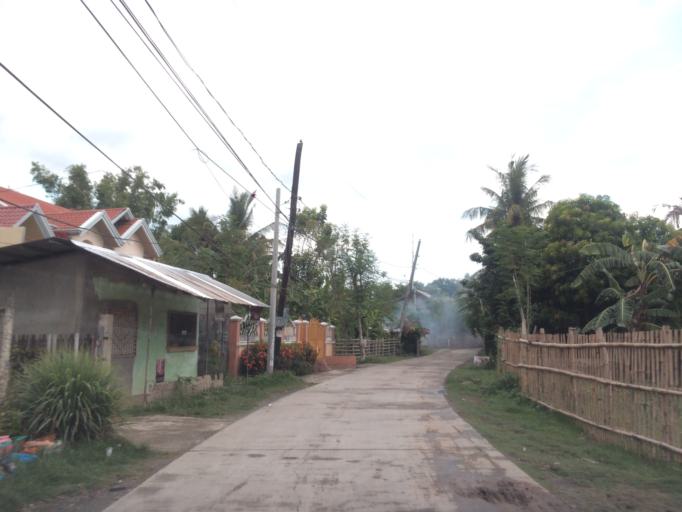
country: PH
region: Ilocos
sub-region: Province of Pangasinan
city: Dumpay
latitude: 15.8799
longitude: 120.3879
